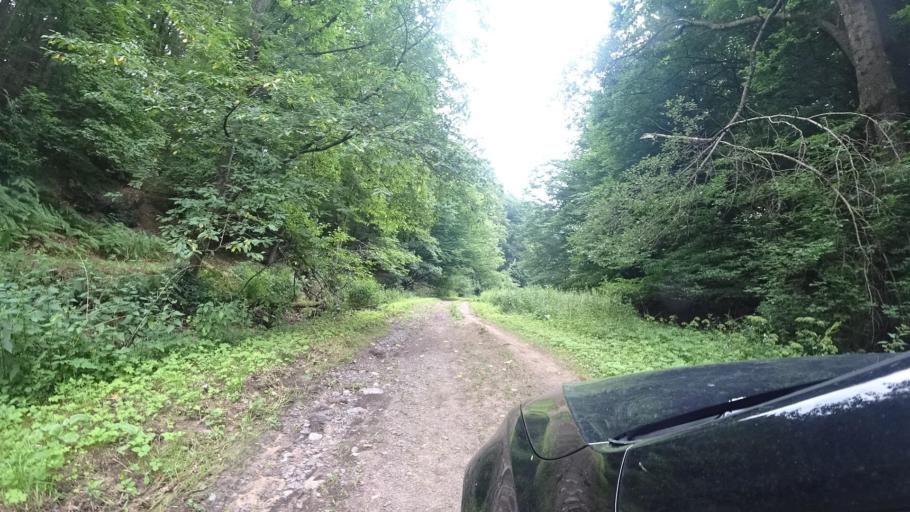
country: DE
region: Rheinland-Pfalz
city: Dorrenbach
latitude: 49.0933
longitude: 7.9770
